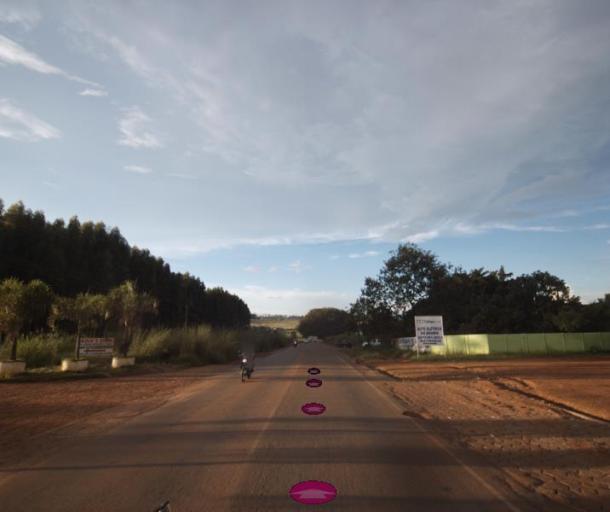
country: BR
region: Goias
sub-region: Anapolis
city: Anapolis
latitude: -16.2808
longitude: -48.9424
